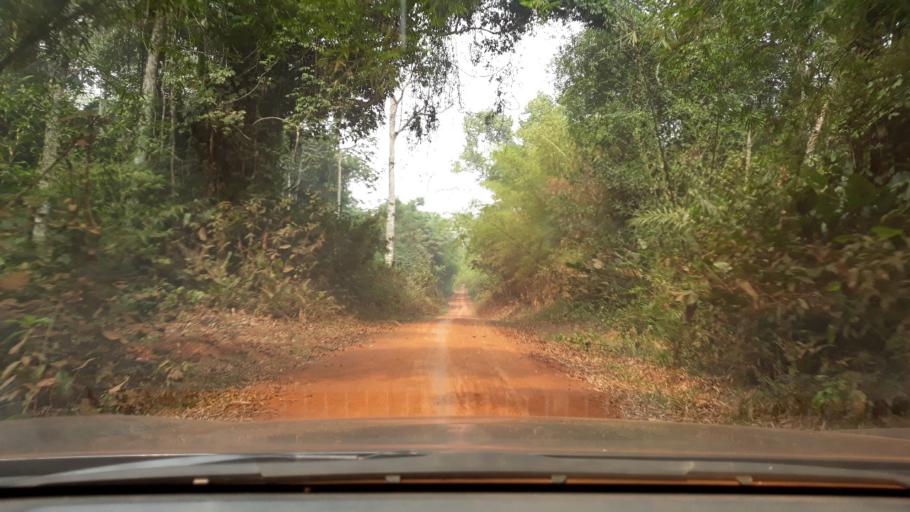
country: CD
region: Eastern Province
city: Aketi
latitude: 2.8863
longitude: 24.0067
